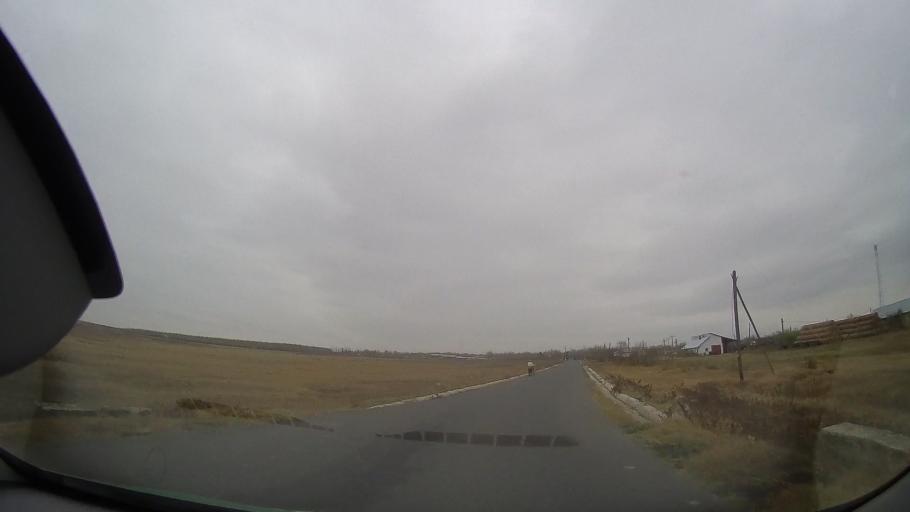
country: RO
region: Braila
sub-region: Comuna Ciocile
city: Ciocile
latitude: 44.8001
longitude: 27.2723
